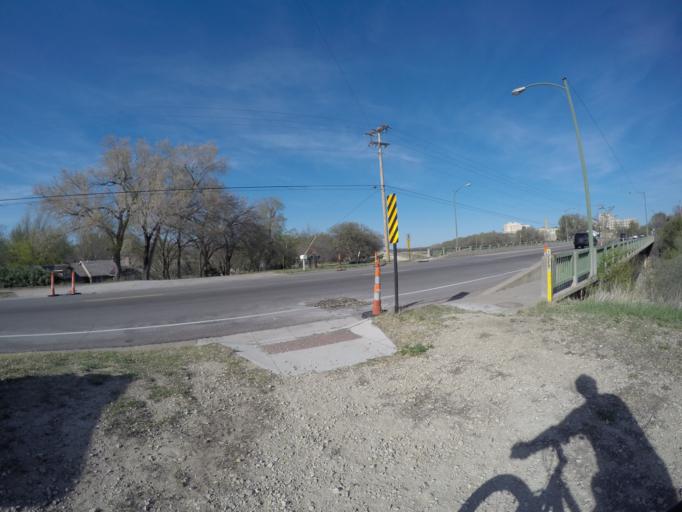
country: US
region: Kansas
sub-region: Saline County
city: Salina
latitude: 38.8403
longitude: -97.5830
